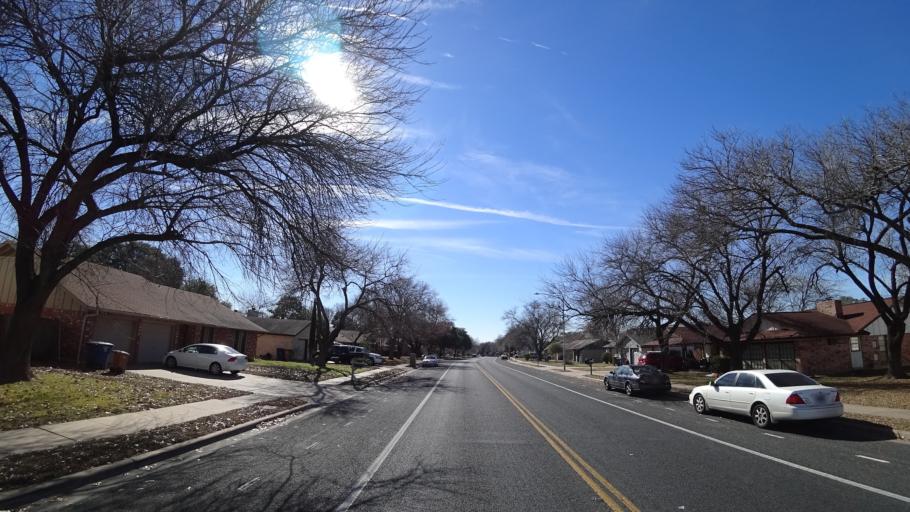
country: US
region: Texas
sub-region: Travis County
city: Wells Branch
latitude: 30.3802
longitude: -97.6984
